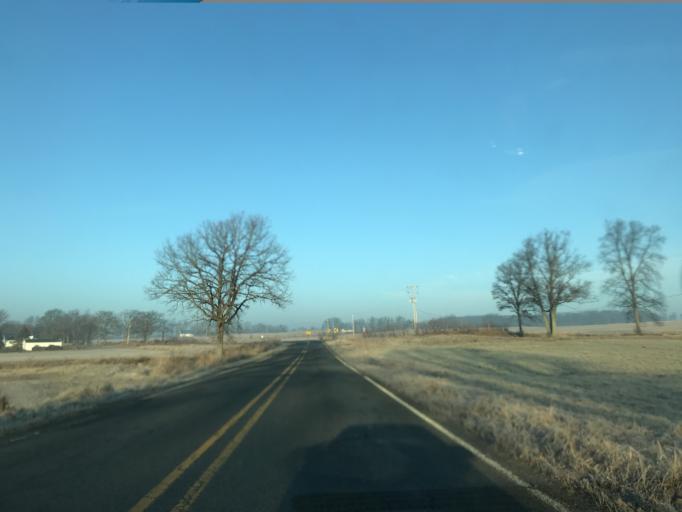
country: US
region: Michigan
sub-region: Ingham County
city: Leslie
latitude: 42.4209
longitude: -84.5160
